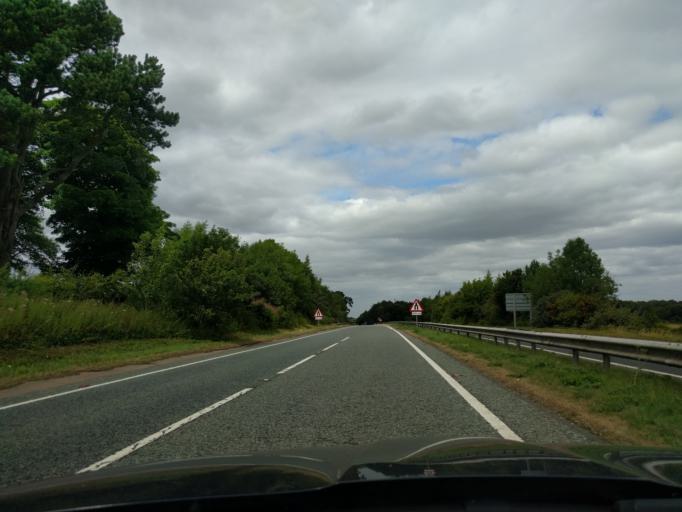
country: GB
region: England
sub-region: Northumberland
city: Ellingham
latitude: 55.5147
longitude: -1.7429
